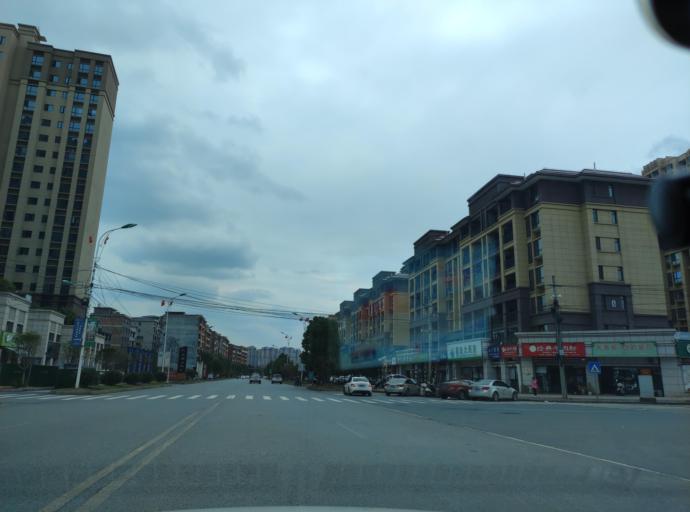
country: CN
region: Jiangxi Sheng
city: Pingxiang
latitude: 27.6765
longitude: 113.9064
